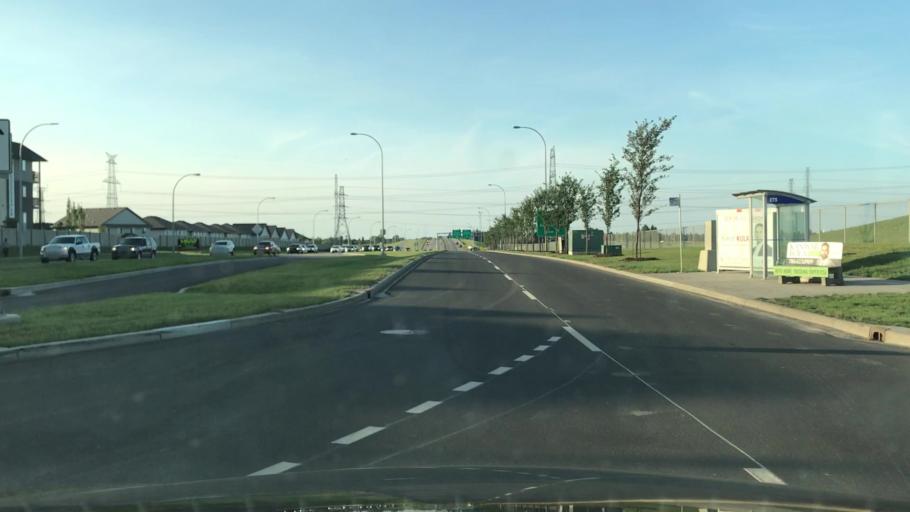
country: CA
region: Alberta
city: Beaumont
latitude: 53.4287
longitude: -113.4178
